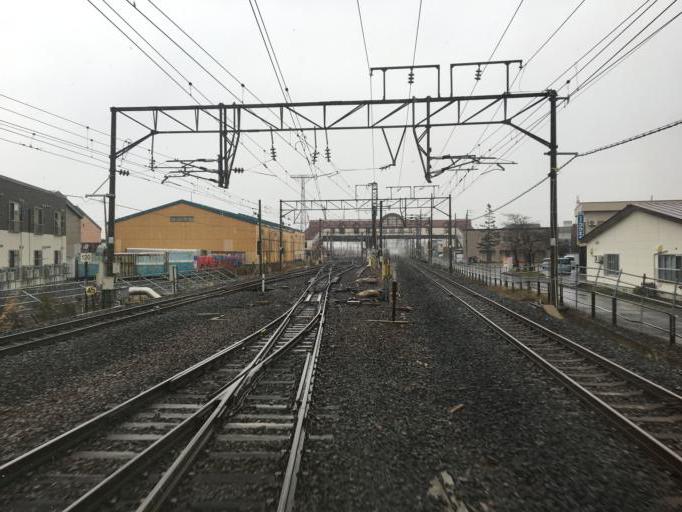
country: JP
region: Aomori
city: Aomori Shi
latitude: 40.8090
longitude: 140.7806
